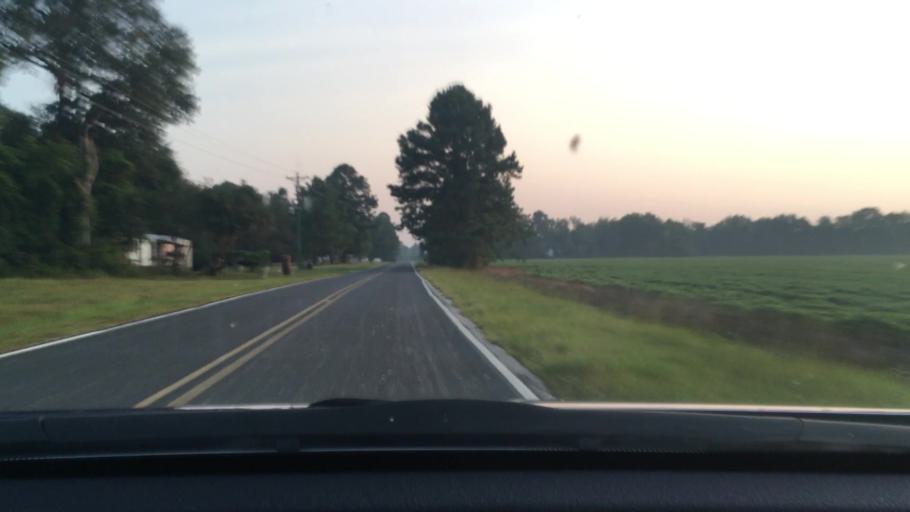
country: US
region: South Carolina
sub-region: Lee County
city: Bishopville
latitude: 34.2308
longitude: -80.1332
